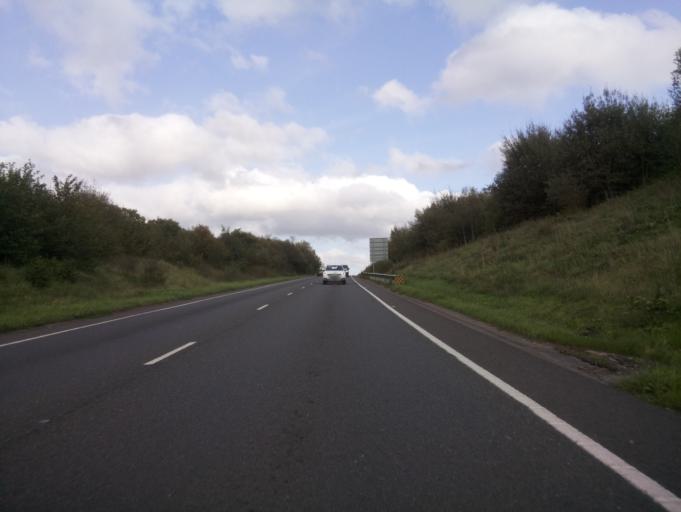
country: GB
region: Wales
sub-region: Rhondda Cynon Taf
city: Beddau
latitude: 51.5449
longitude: -3.3540
